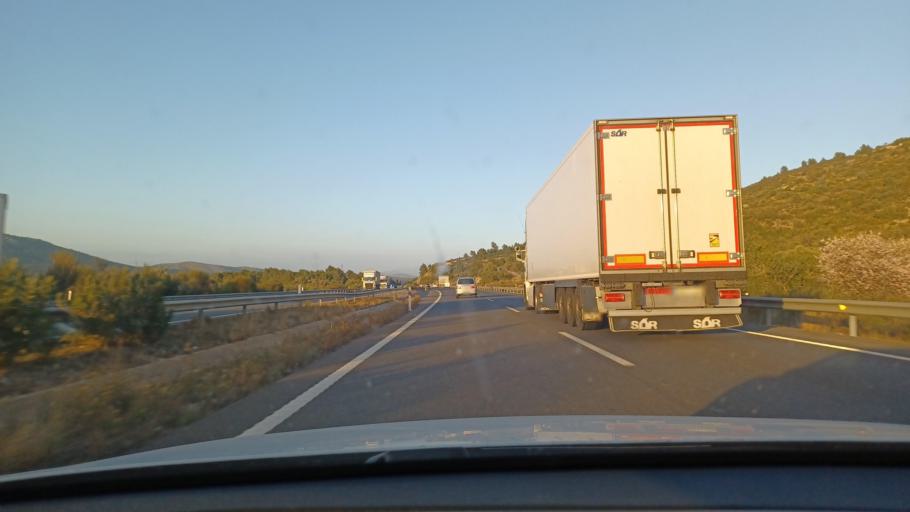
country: ES
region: Valencia
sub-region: Provincia de Castello
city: Santa Magdalena de Pulpis
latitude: 40.3786
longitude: 0.3413
